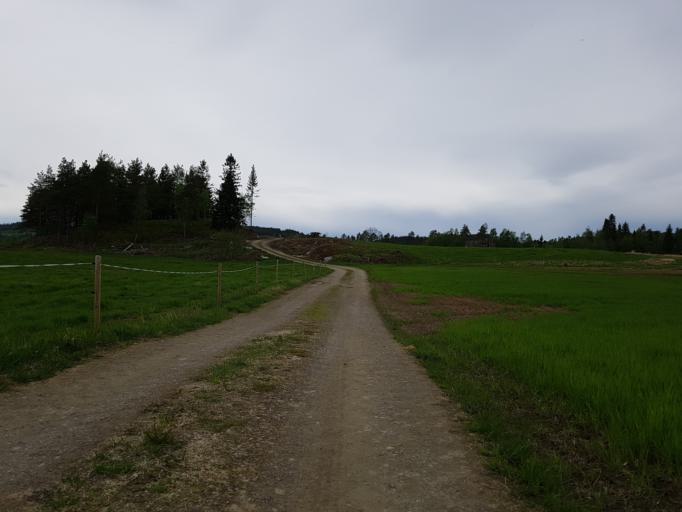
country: NO
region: Nord-Trondelag
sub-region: Levanger
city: Skogn
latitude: 63.6305
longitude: 11.2587
